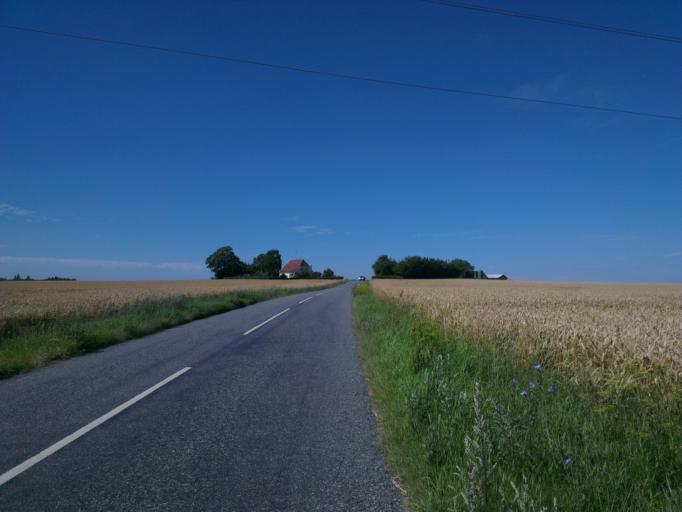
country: DK
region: Capital Region
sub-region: Frederikssund Kommune
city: Frederikssund
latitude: 55.8649
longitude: 12.0930
